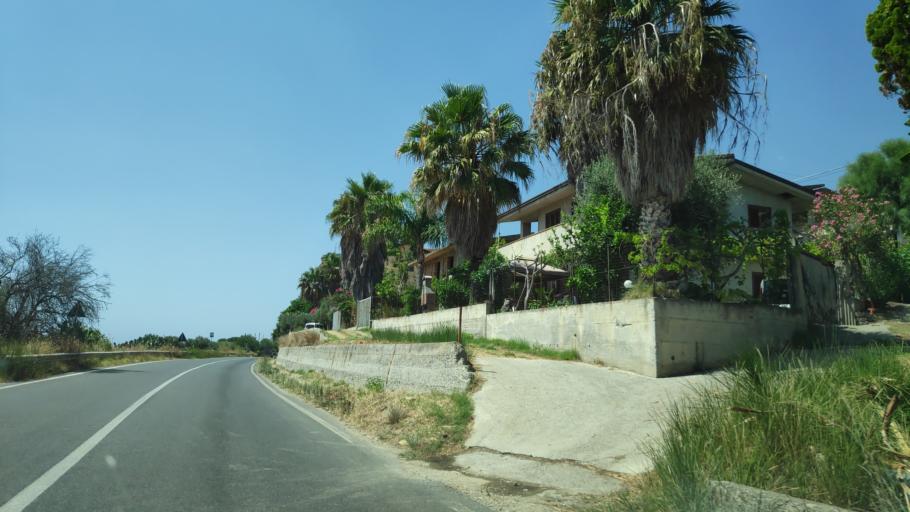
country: IT
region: Calabria
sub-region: Provincia di Reggio Calabria
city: Weather Station
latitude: 37.9393
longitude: 16.0776
